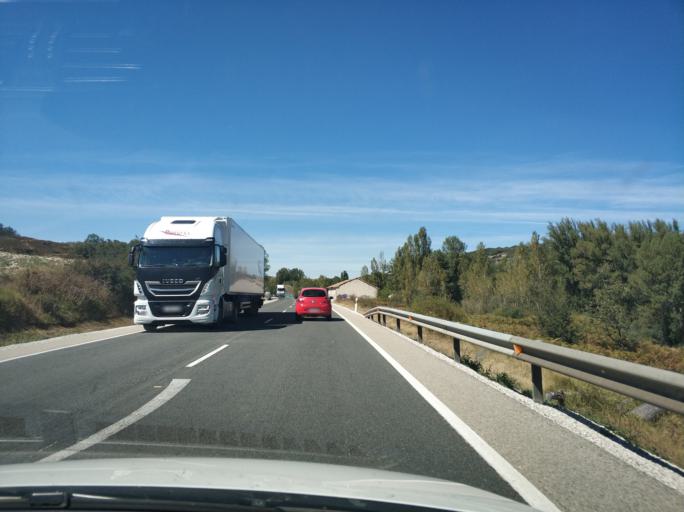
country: ES
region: Castille and Leon
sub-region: Provincia de Burgos
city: Basconcillos del Tozo
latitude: 42.7149
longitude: -4.0190
